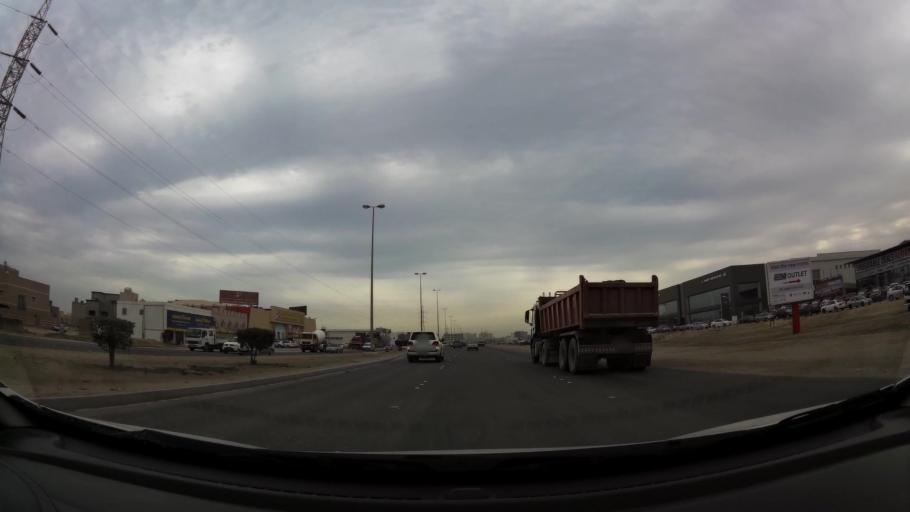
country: BH
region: Northern
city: Sitrah
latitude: 26.1558
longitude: 50.6099
